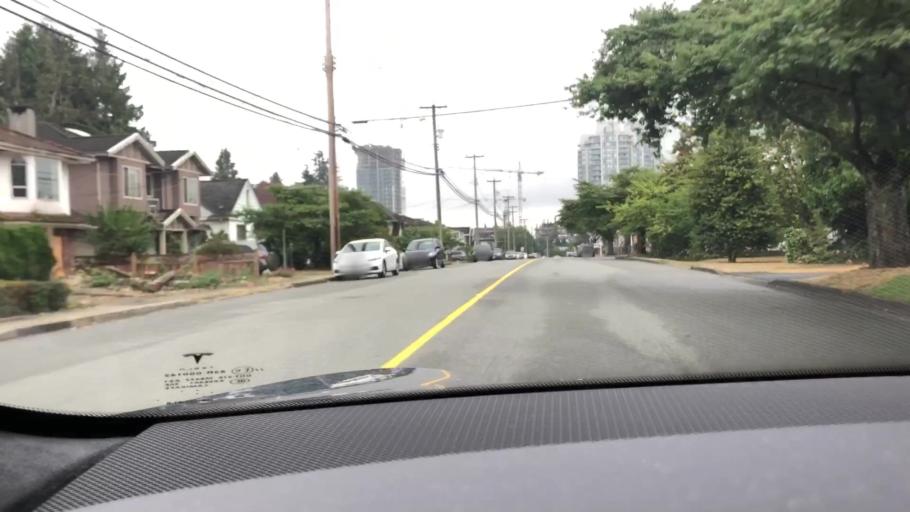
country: CA
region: British Columbia
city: Burnaby
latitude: 49.2227
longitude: -122.9557
